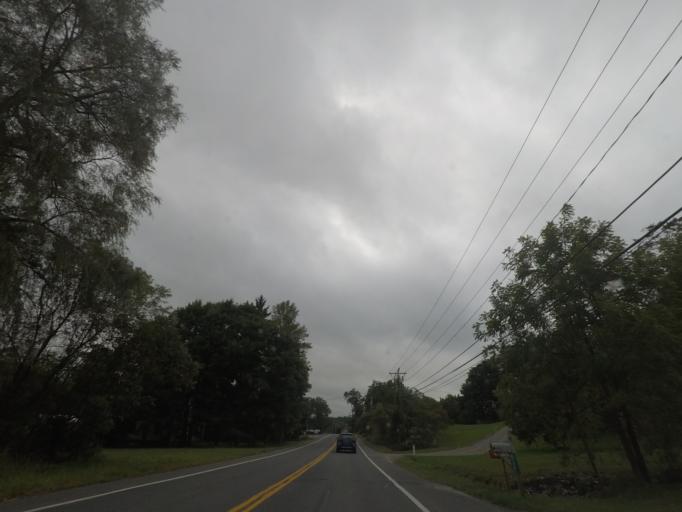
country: US
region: New York
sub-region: Rensselaer County
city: Hoosick Falls
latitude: 42.8885
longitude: -73.3602
